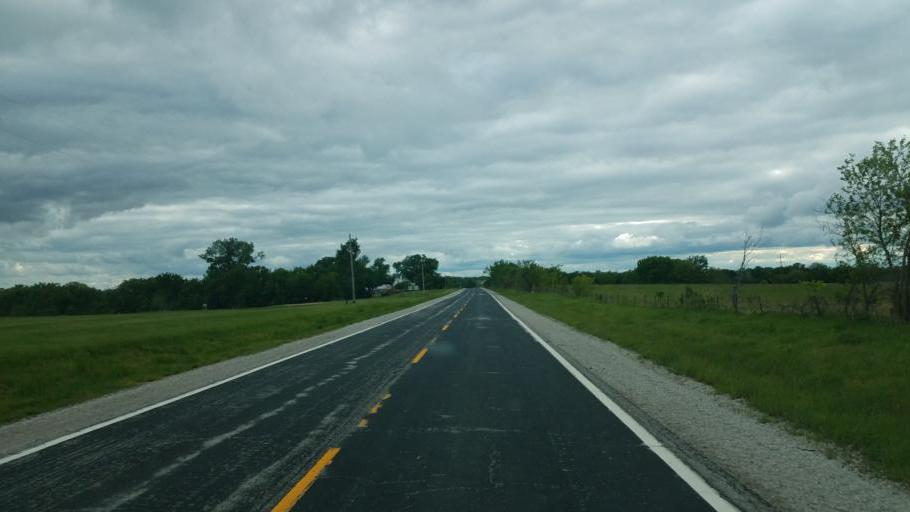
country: US
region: Missouri
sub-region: Mercer County
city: Princeton
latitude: 40.3818
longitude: -93.6824
